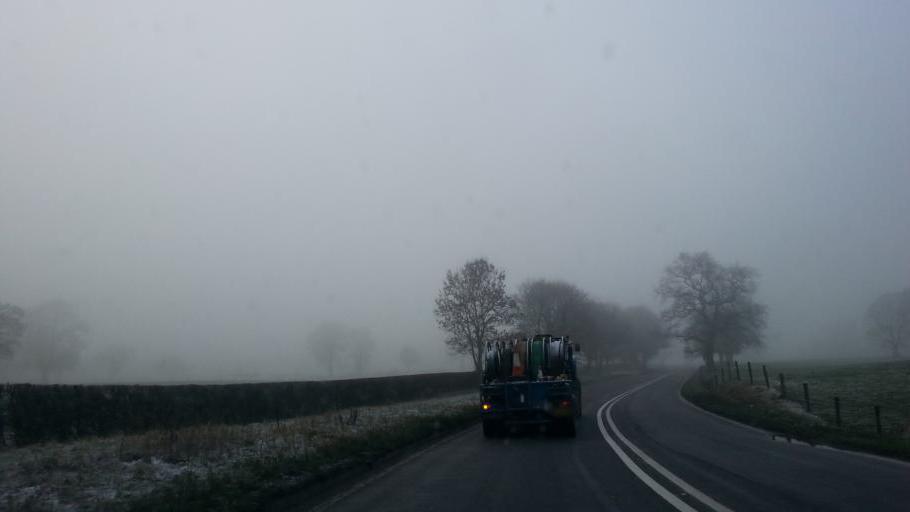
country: GB
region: England
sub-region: Cheshire East
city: Siddington
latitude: 53.2208
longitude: -2.2367
